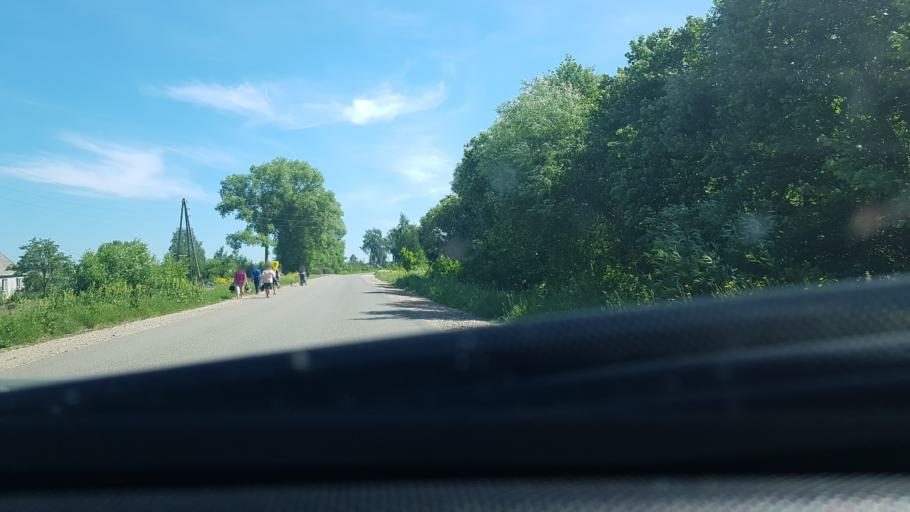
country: LV
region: Daugavpils
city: Daugavpils
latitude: 55.8570
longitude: 26.5739
